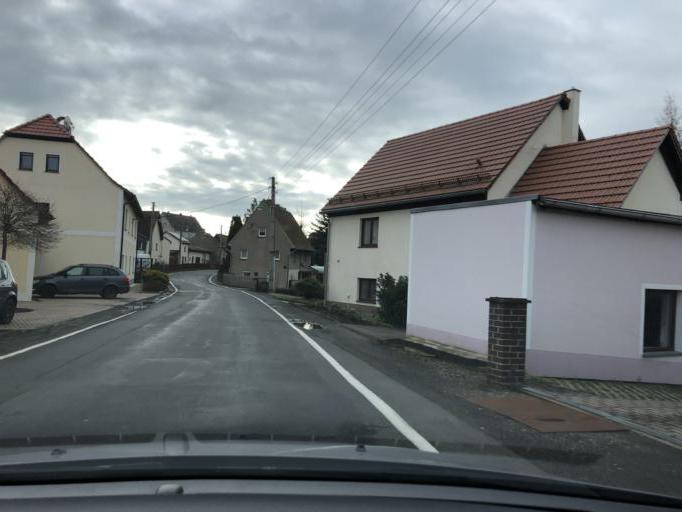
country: DE
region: Saxony
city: Ostrau
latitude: 51.2033
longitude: 12.8319
